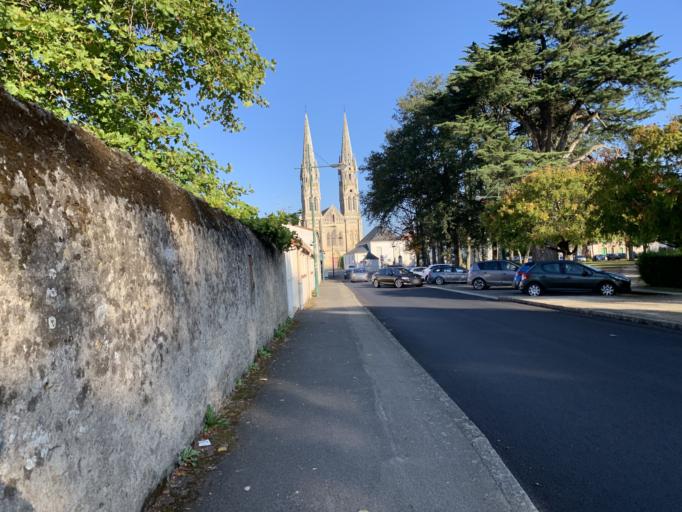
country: FR
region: Pays de la Loire
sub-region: Departement de la Loire-Atlantique
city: Machecoul
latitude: 46.9912
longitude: -1.8164
